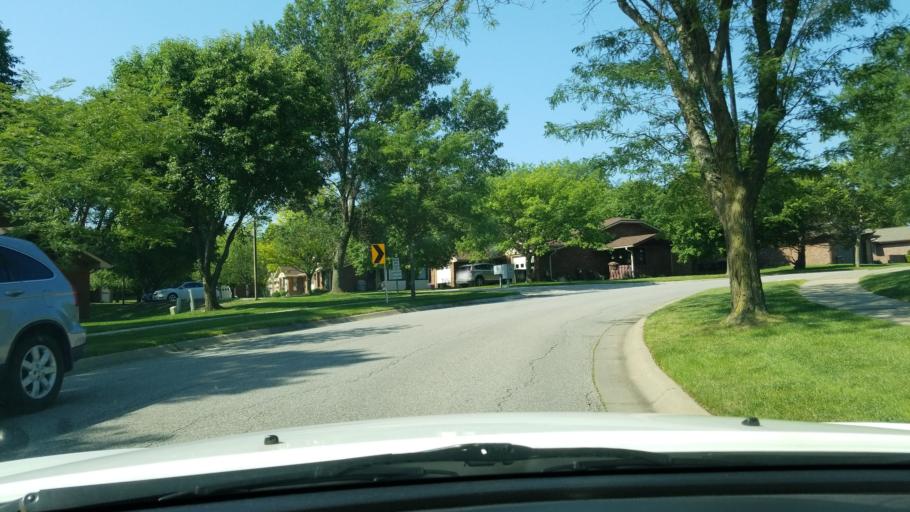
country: US
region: Nebraska
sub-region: Lancaster County
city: Lincoln
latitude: 40.8020
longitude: -96.6282
